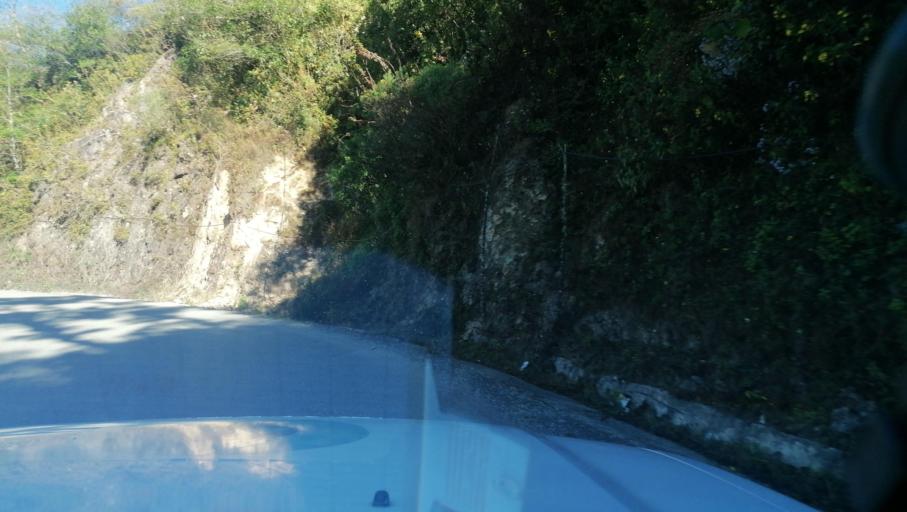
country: MX
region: Chiapas
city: Motozintla de Mendoza
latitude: 15.2702
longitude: -92.2280
